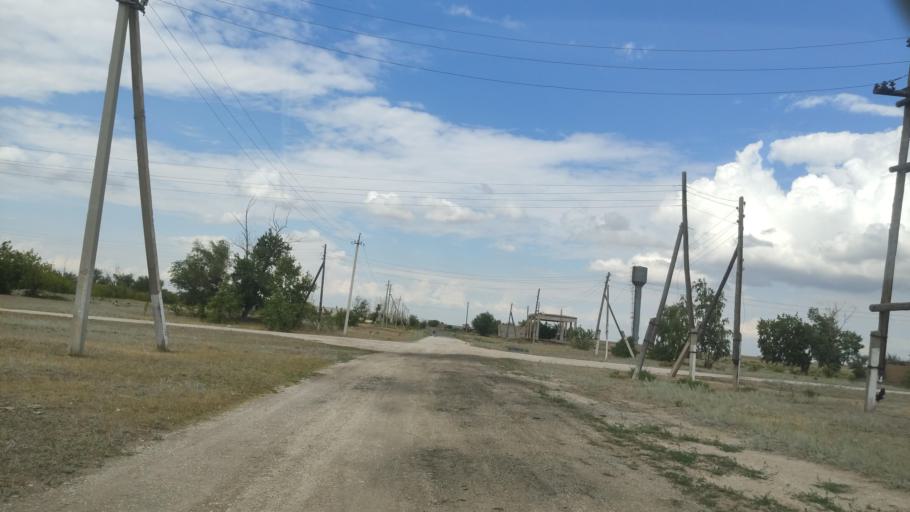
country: KZ
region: Pavlodar
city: Pavlodar
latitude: 52.6488
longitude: 77.0233
